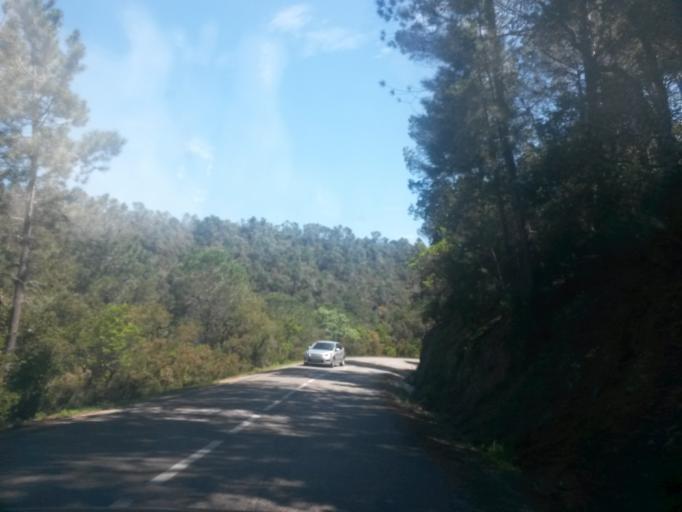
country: ES
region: Catalonia
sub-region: Provincia de Girona
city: Madremanya
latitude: 41.9831
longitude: 2.9410
